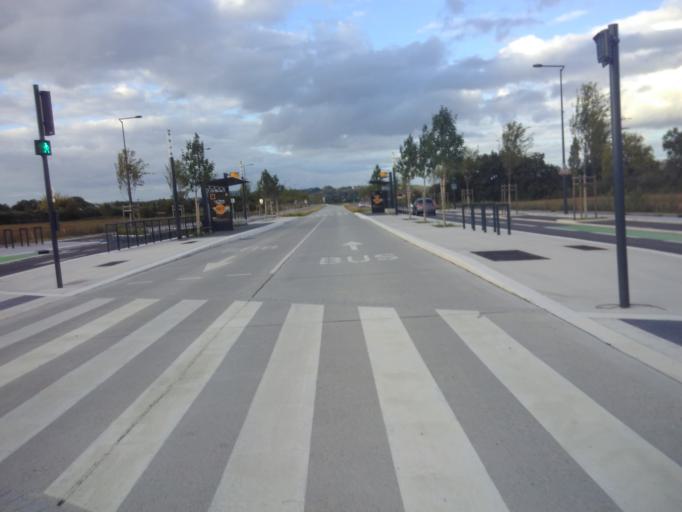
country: FR
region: Midi-Pyrenees
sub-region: Departement de la Haute-Garonne
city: Launaguet
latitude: 43.6498
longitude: 1.4562
